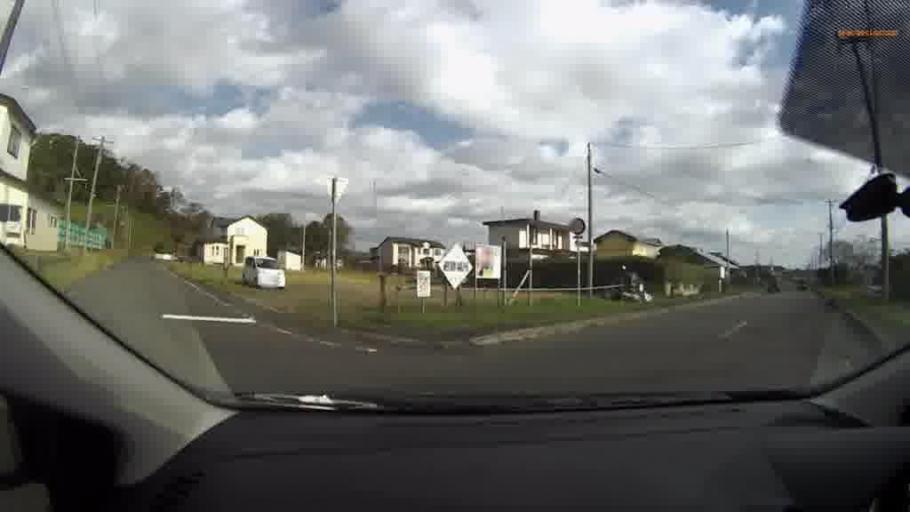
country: JP
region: Hokkaido
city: Kushiro
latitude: 42.9756
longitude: 144.1227
